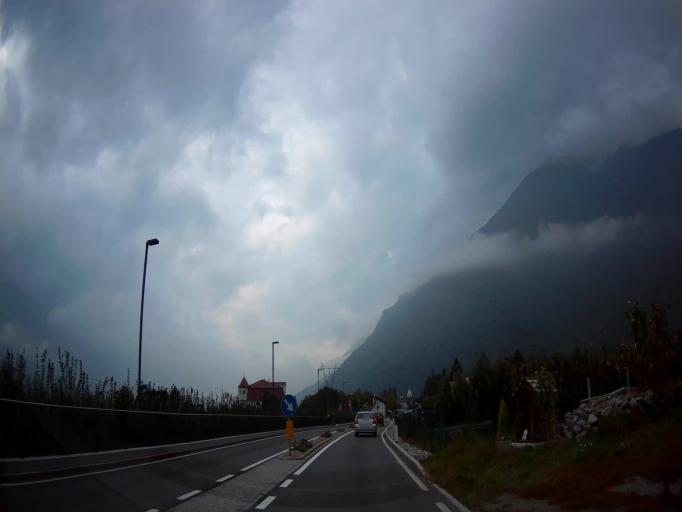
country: IT
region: Trentino-Alto Adige
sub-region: Bolzano
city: Rabla
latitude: 46.6708
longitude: 11.0670
